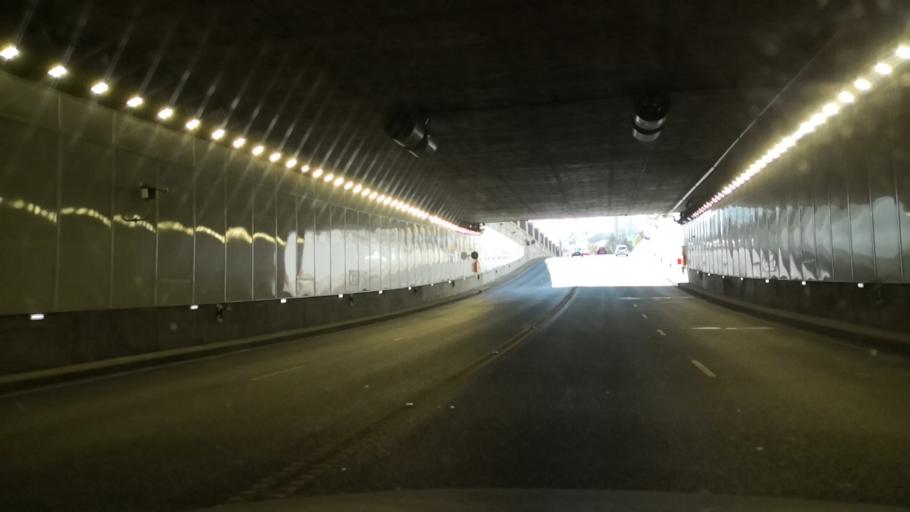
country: ES
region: Galicia
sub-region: Provincia da Coruna
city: A Coruna
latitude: 43.3680
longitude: -8.3987
